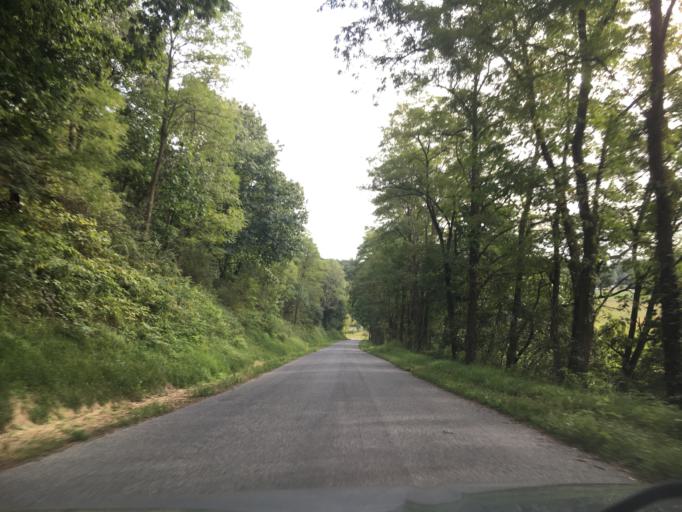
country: US
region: Pennsylvania
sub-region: Berks County
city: Topton
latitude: 40.6114
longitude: -75.7148
